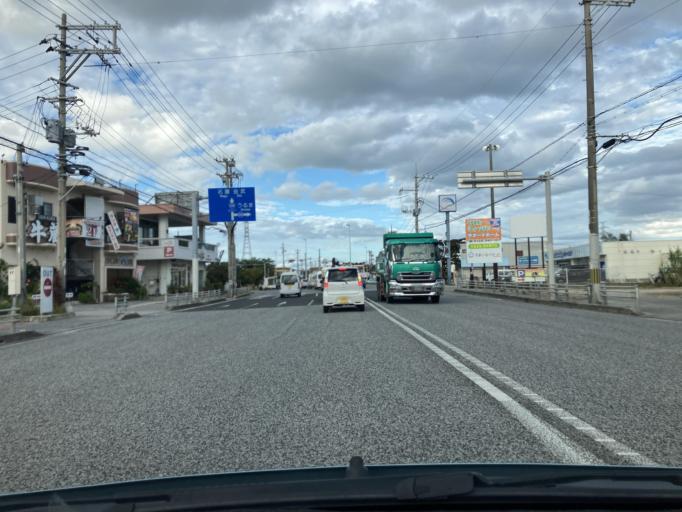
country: JP
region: Okinawa
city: Ishikawa
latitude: 26.3870
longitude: 127.8282
